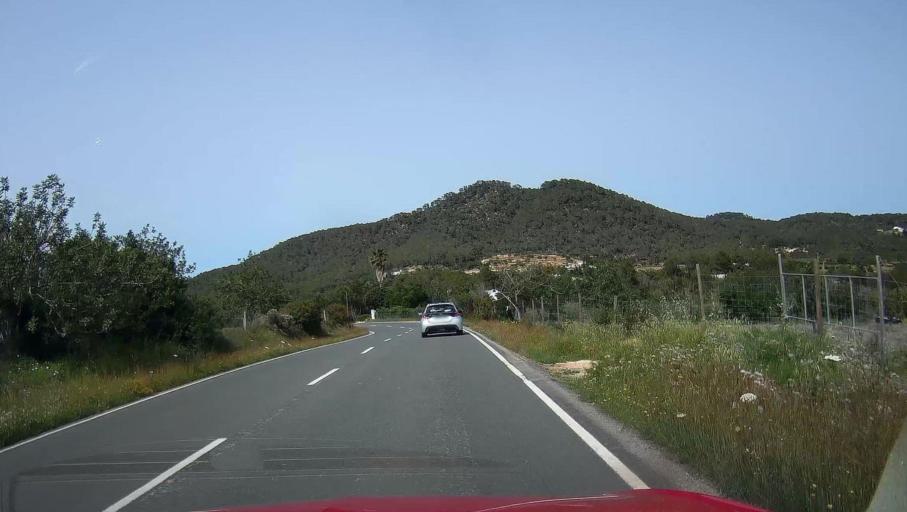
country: ES
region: Balearic Islands
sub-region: Illes Balears
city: Sant Joan de Labritja
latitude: 39.0862
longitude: 1.5015
